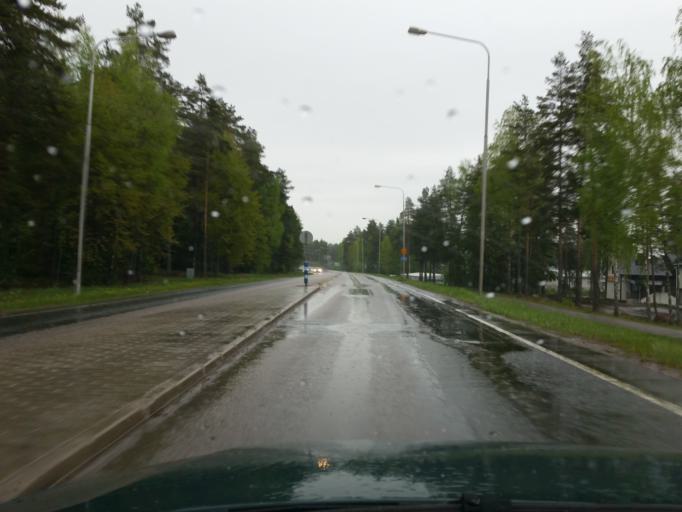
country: FI
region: Uusimaa
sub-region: Helsinki
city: Lohja
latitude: 60.2797
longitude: 24.1530
